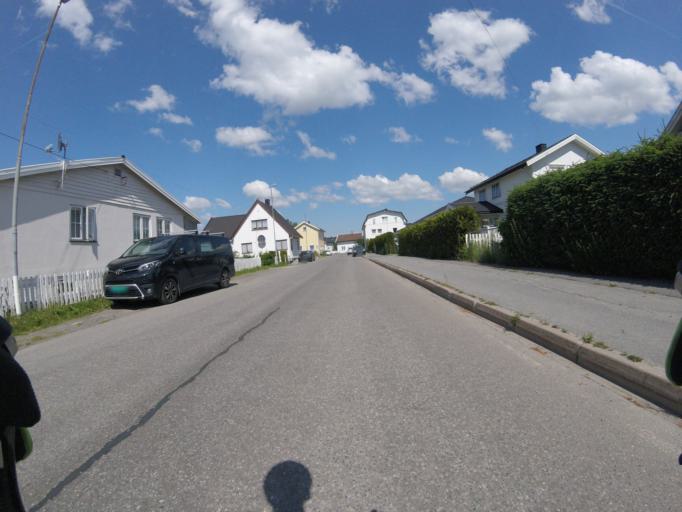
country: NO
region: Akershus
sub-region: Skedsmo
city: Lillestrom
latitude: 59.9507
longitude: 11.0605
